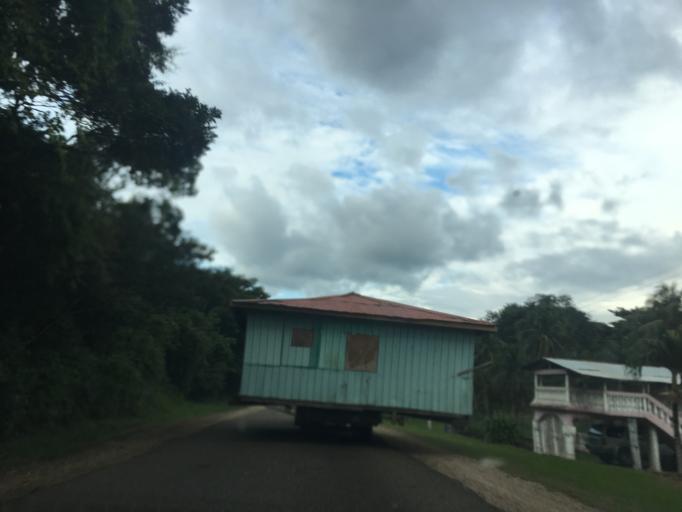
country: BZ
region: Cayo
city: San Ignacio
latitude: 17.2058
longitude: -88.9440
